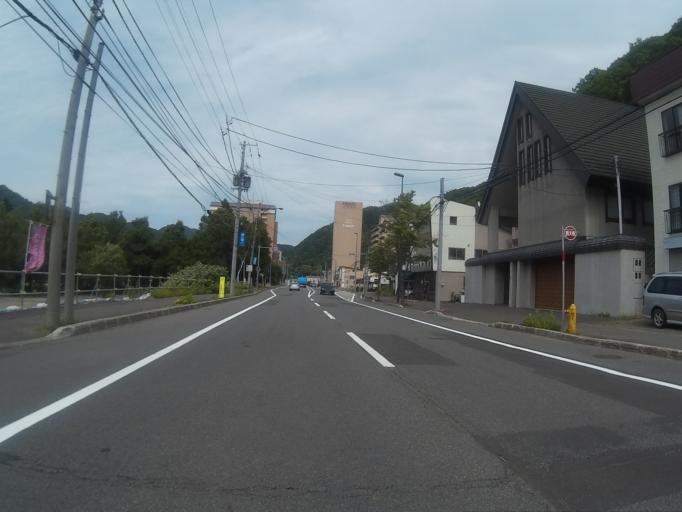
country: JP
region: Hokkaido
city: Sapporo
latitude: 42.9620
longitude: 141.1594
